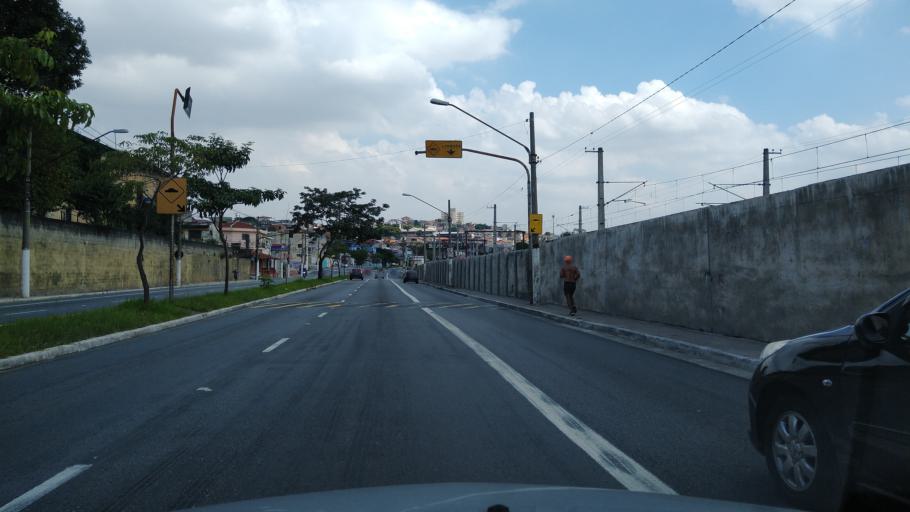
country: BR
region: Sao Paulo
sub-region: Guarulhos
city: Guarulhos
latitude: -23.5070
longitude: -46.5420
